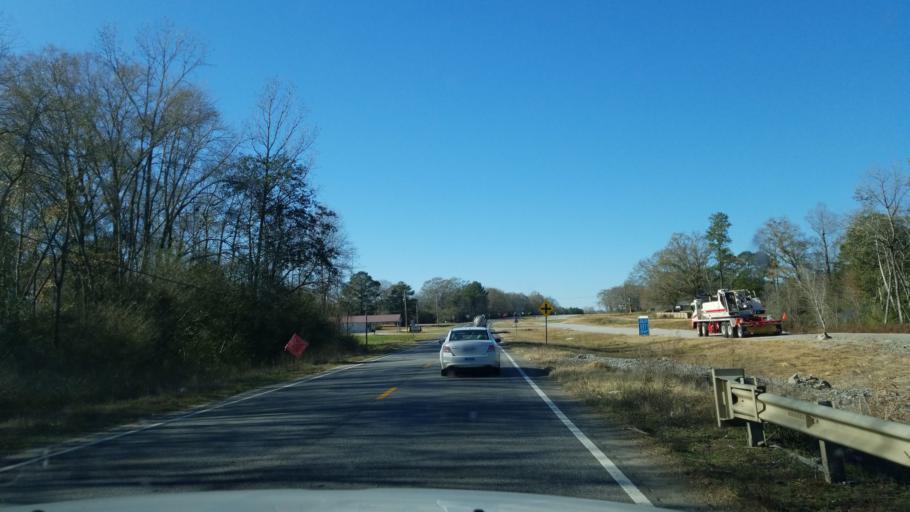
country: US
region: Alabama
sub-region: Pickens County
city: Gordo
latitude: 33.3350
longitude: -87.9272
